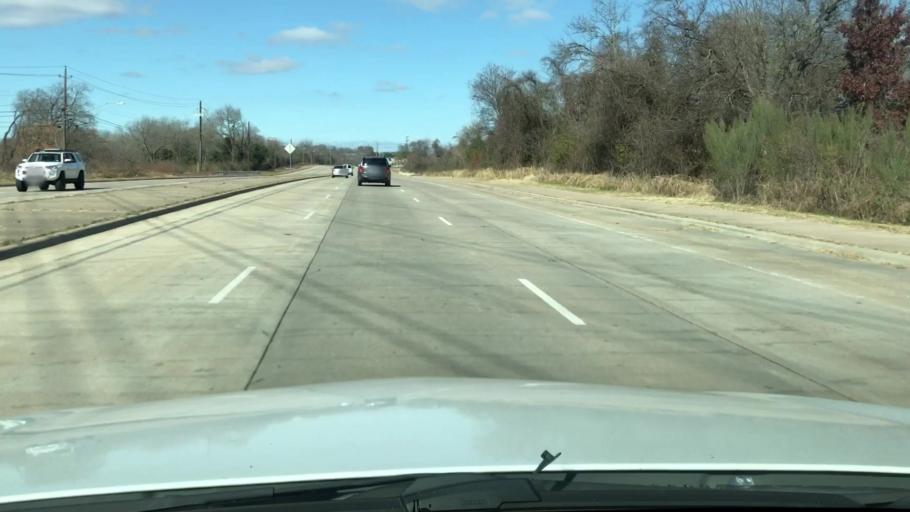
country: US
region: Texas
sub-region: Travis County
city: Onion Creek
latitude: 30.1721
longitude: -97.7402
